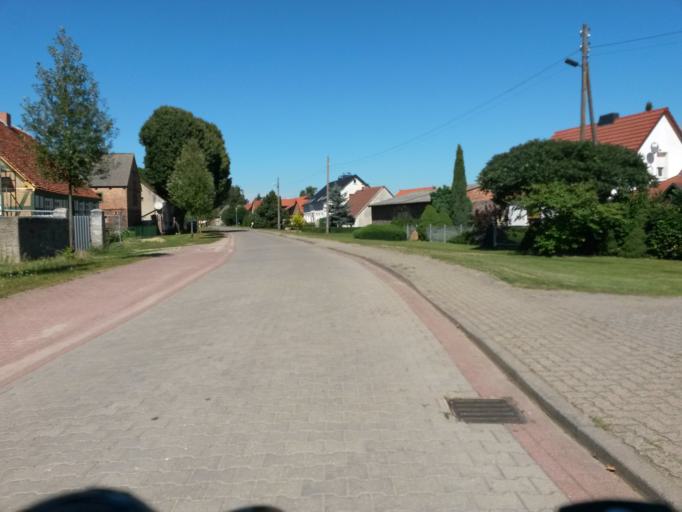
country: DE
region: Brandenburg
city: Schoneberg
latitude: 52.9232
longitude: 14.1213
